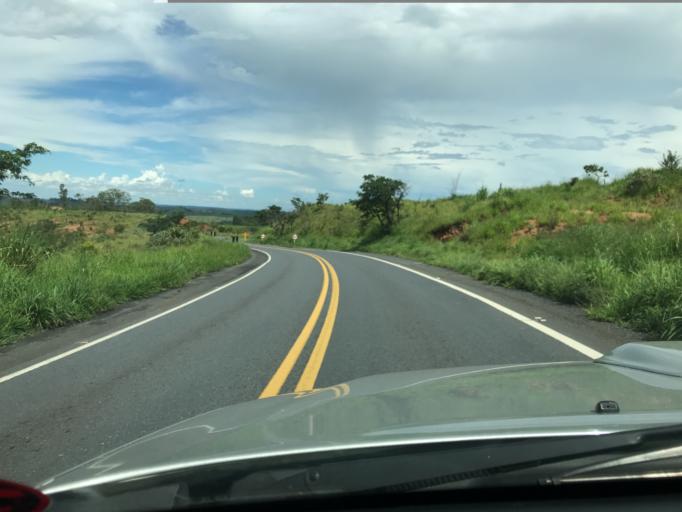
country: BR
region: Minas Gerais
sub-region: Campos Altos
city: Campos Altos
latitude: -19.7947
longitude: -46.0372
